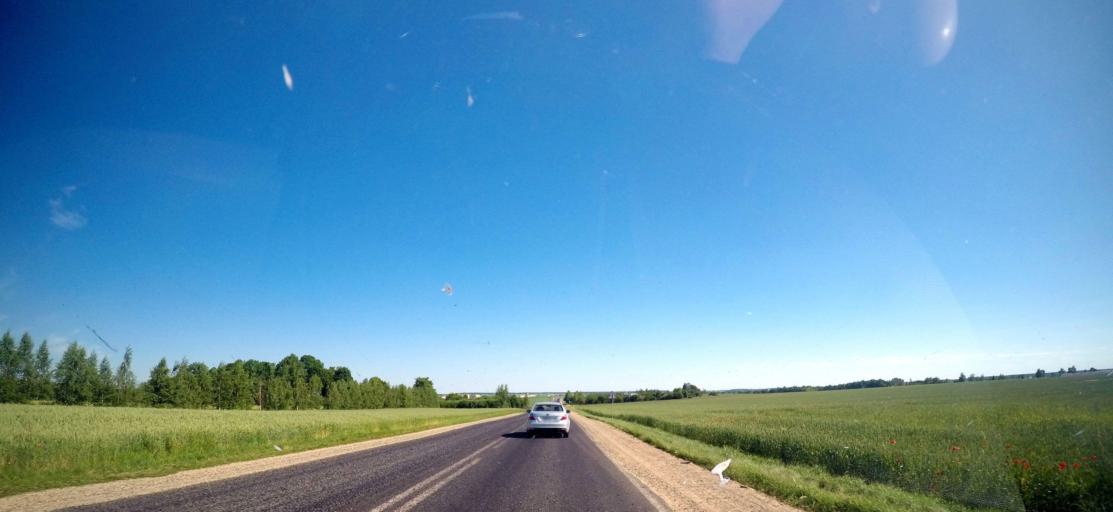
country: BY
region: Grodnenskaya
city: Vyalikaya Byerastavitsa
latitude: 53.2143
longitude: 24.0014
